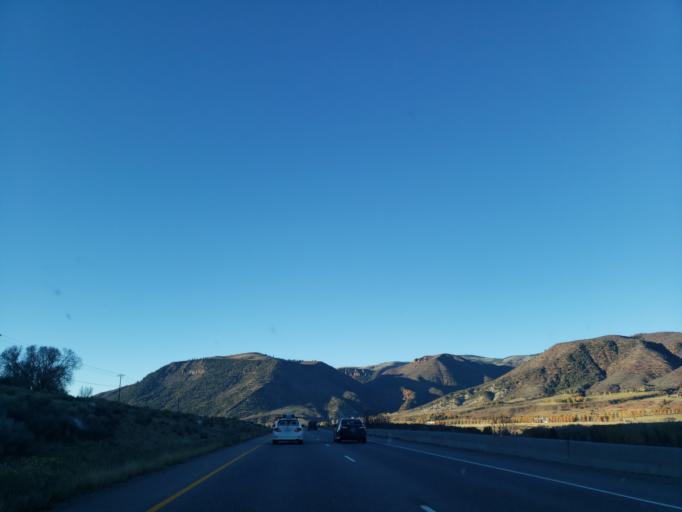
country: US
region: Colorado
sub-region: Pitkin County
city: Snowmass Village
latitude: 39.2722
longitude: -106.8916
